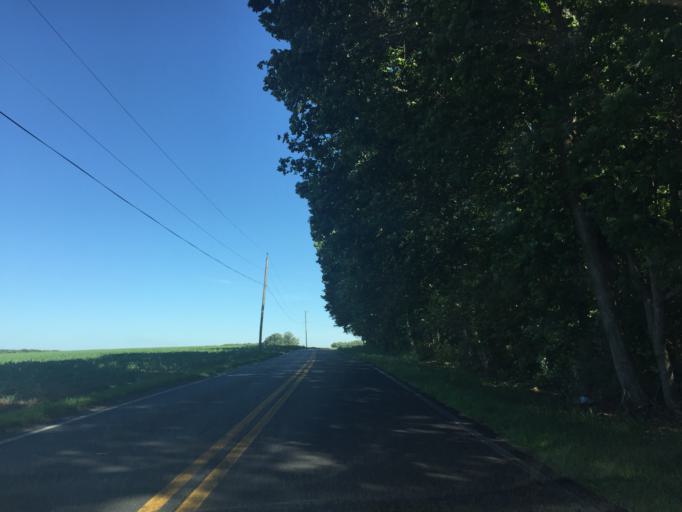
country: US
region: Maryland
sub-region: Carroll County
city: Hampstead
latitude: 39.5768
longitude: -76.9196
